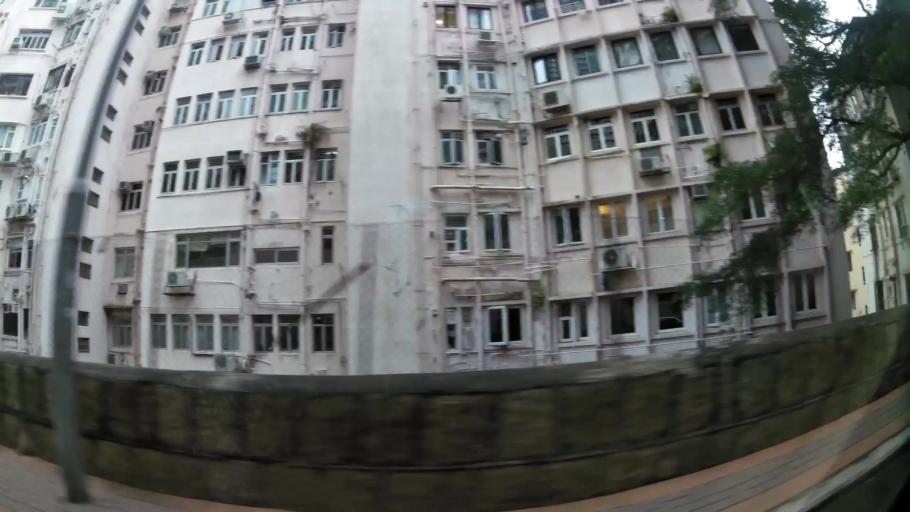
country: HK
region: Central and Western
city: Central
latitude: 22.2755
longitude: 114.1603
